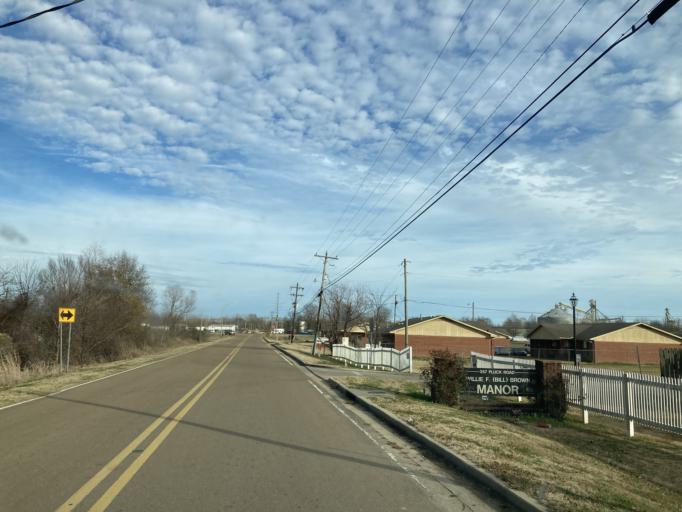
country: US
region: Mississippi
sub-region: Humphreys County
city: Belzoni
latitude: 33.1676
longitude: -90.5012
